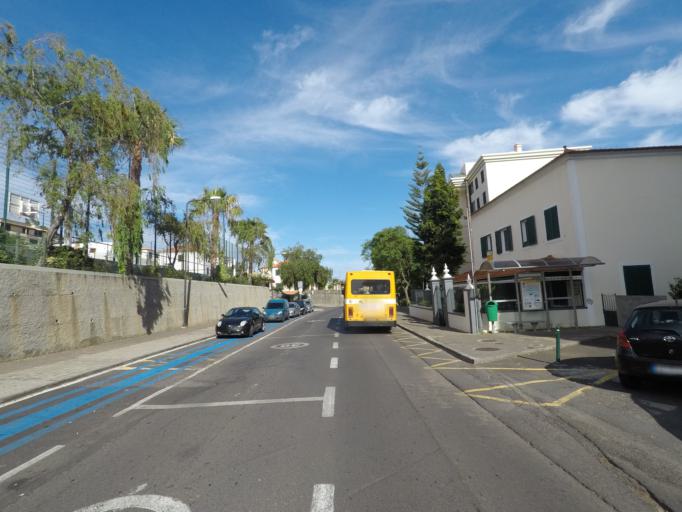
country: PT
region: Madeira
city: Camara de Lobos
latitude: 32.6390
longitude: -16.9421
